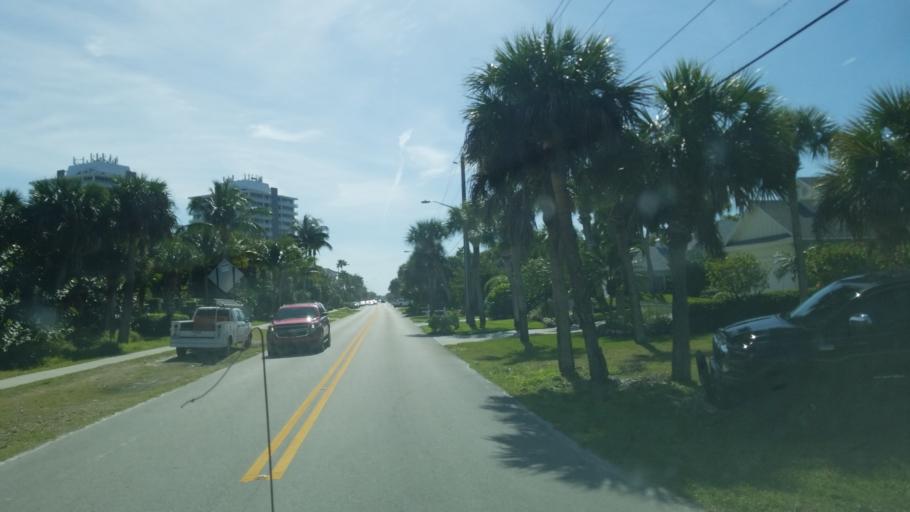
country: US
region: Florida
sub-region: Indian River County
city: Vero Beach
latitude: 27.6585
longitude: -80.3581
